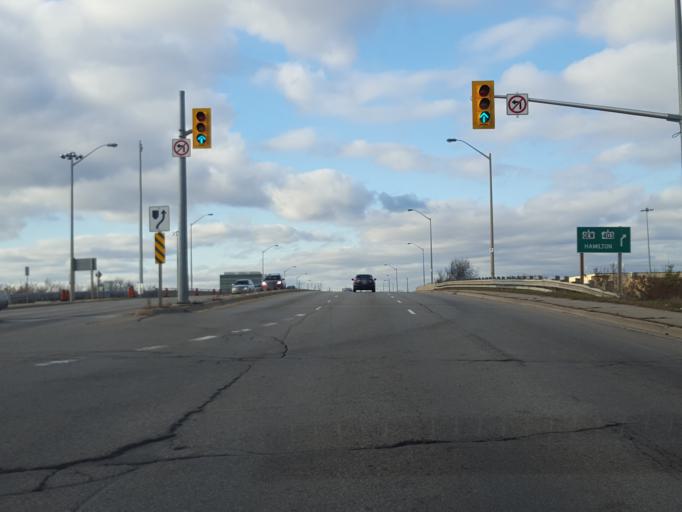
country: CA
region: Ontario
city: Burlington
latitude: 43.3654
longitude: -79.7866
